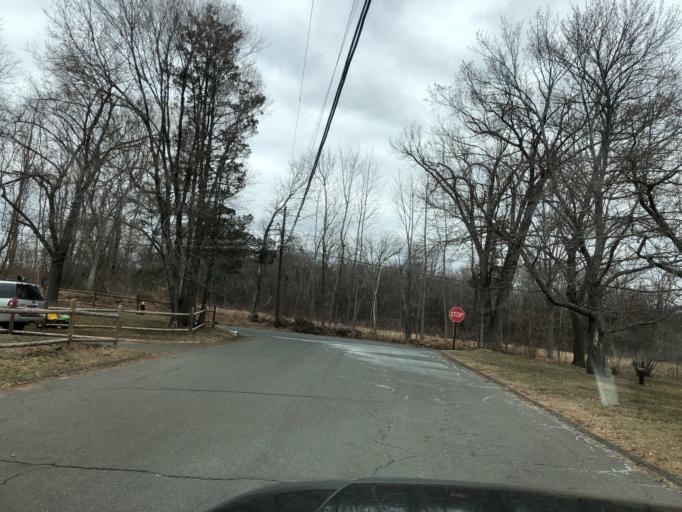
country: US
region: Connecticut
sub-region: Hartford County
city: Plainville
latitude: 41.6285
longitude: -72.8927
